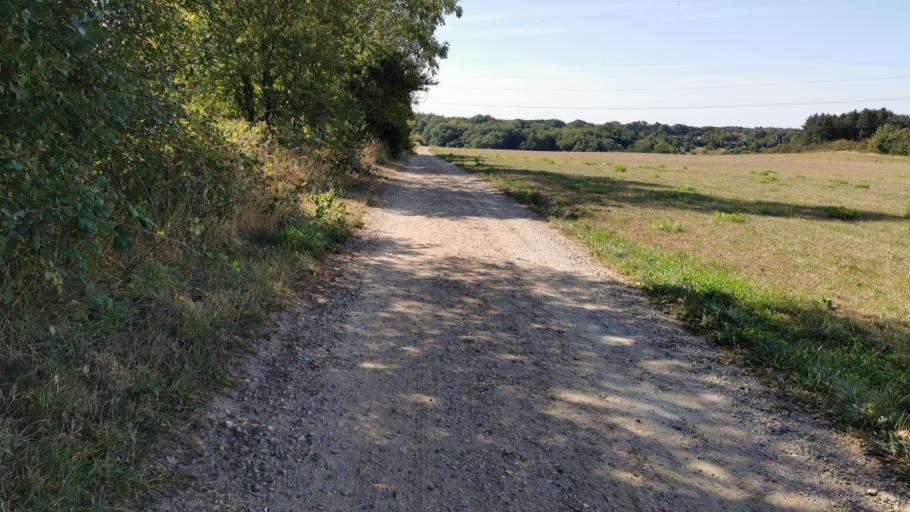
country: DK
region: South Denmark
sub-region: Kolding Kommune
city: Kolding
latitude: 55.4806
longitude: 9.4345
